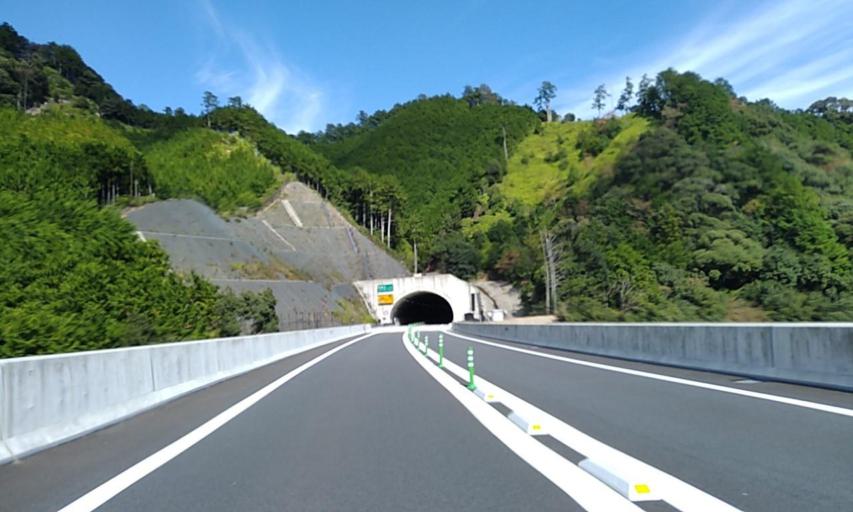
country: JP
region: Mie
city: Owase
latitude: 34.0664
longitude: 136.1721
